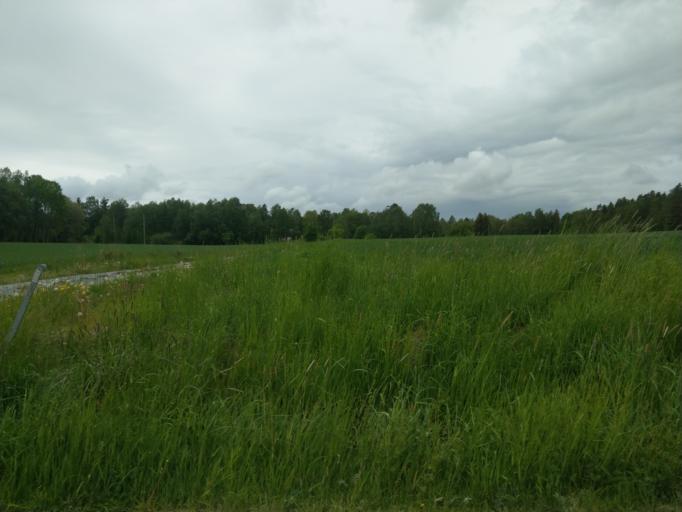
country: SE
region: Stockholm
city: Stenhamra
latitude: 59.4139
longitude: 17.6171
